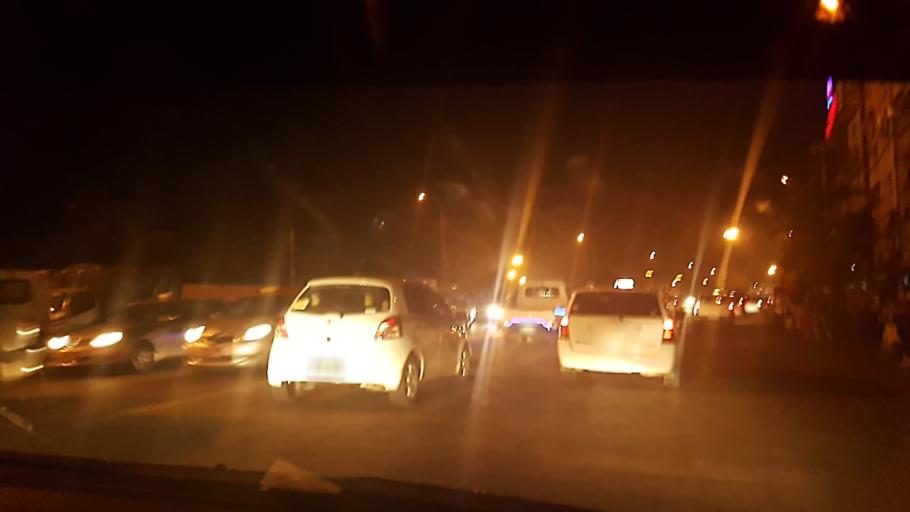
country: MM
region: Yangon
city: Yangon
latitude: 16.7724
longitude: 96.1468
